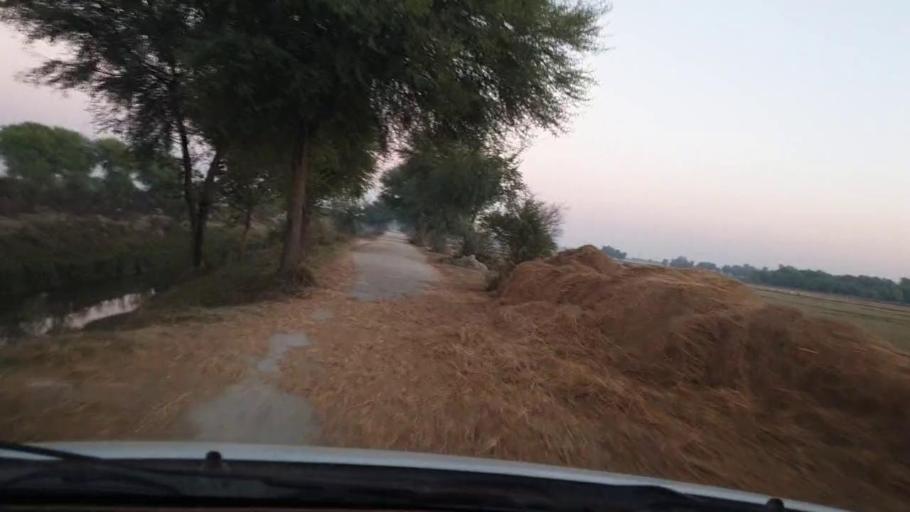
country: PK
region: Sindh
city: Khairpur Nathan Shah
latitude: 27.1500
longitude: 67.6943
